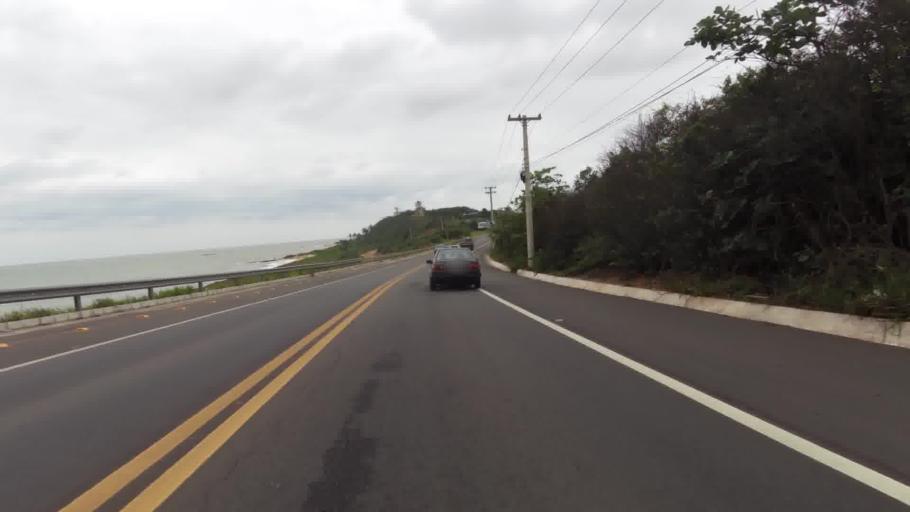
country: BR
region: Espirito Santo
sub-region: Piuma
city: Piuma
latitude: -20.8147
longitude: -40.6139
